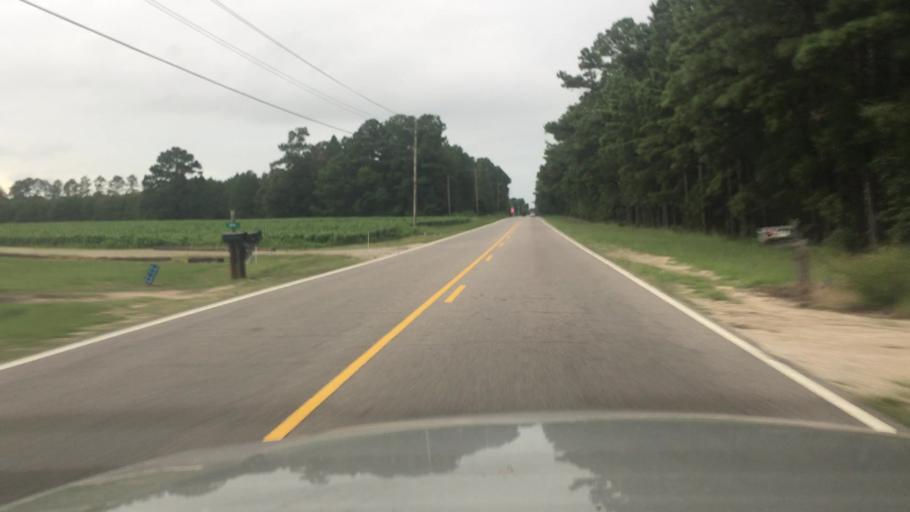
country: US
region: North Carolina
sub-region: Hoke County
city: Rockfish
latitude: 34.9737
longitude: -79.0560
